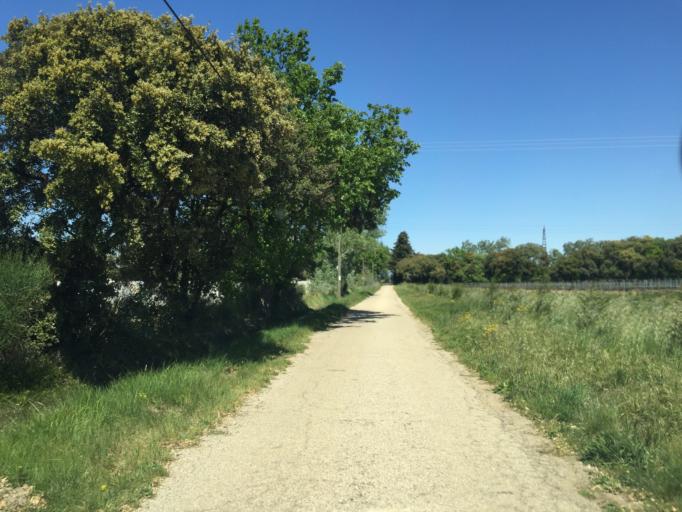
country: FR
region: Provence-Alpes-Cote d'Azur
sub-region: Departement du Vaucluse
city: Jonquieres
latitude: 44.1440
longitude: 4.9200
